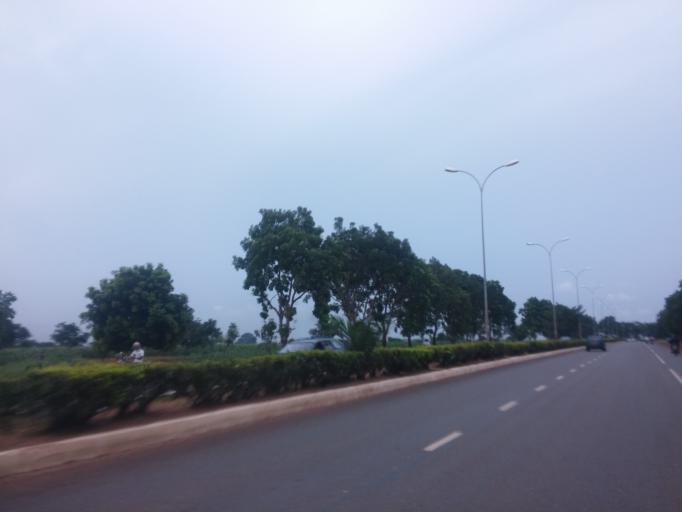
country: TG
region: Maritime
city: Lome
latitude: 6.1949
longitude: 1.2153
